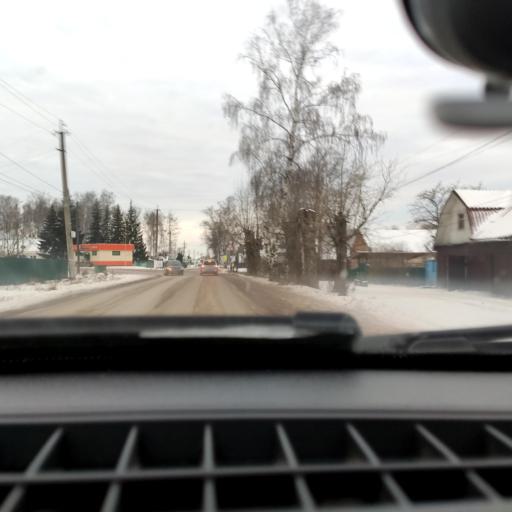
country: RU
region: Bashkortostan
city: Iglino
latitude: 54.8342
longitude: 56.4236
